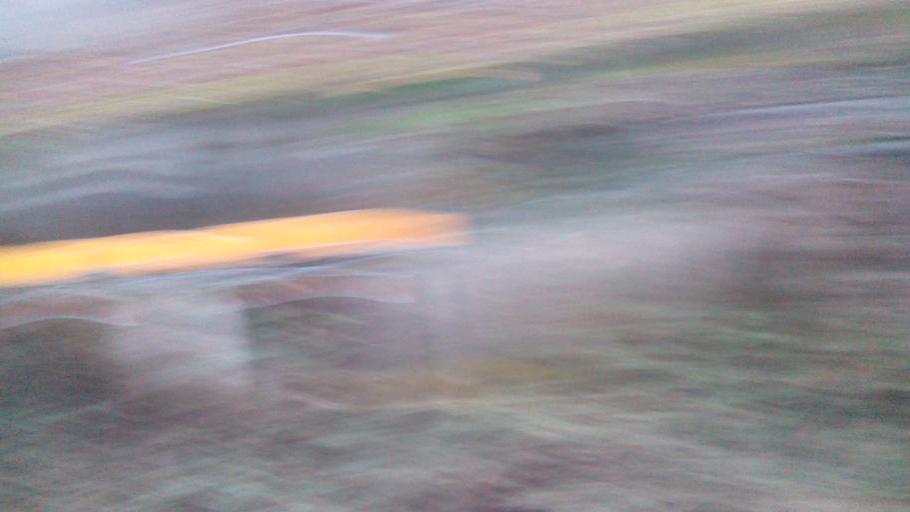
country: TW
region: Taiwan
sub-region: Hualien
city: Hualian
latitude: 24.3474
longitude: 121.3206
